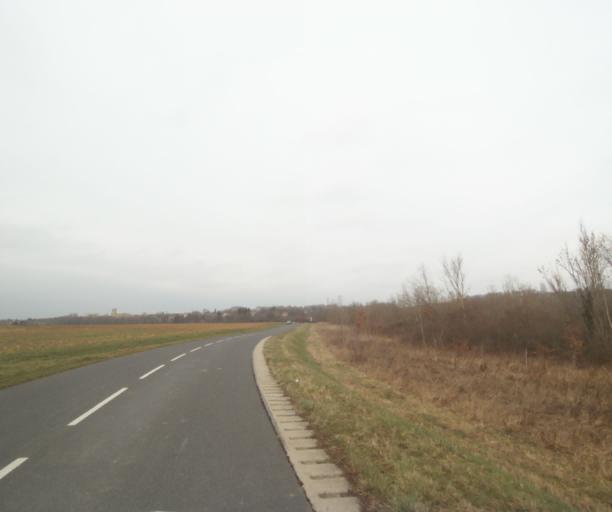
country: FR
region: Champagne-Ardenne
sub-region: Departement de la Marne
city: Pargny-sur-Saulx
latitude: 48.7430
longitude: 4.8603
